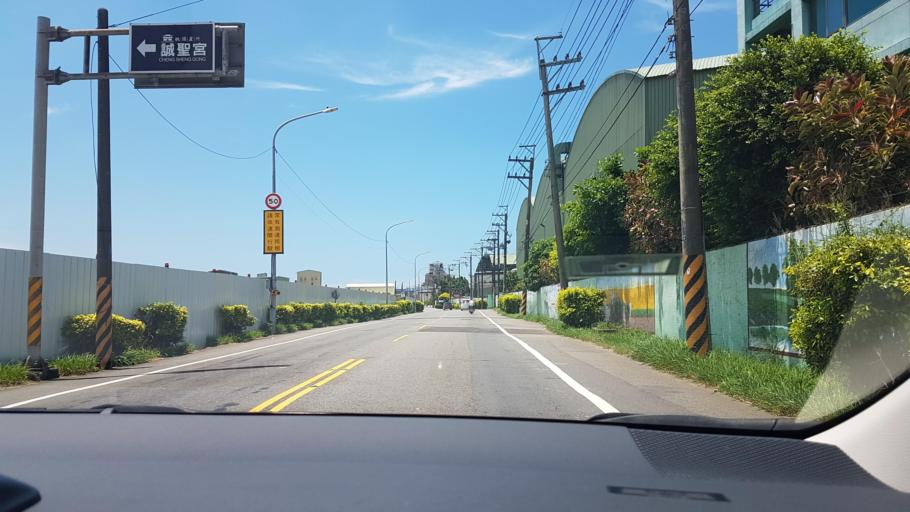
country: TW
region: Taiwan
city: Taoyuan City
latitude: 25.0908
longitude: 121.2740
